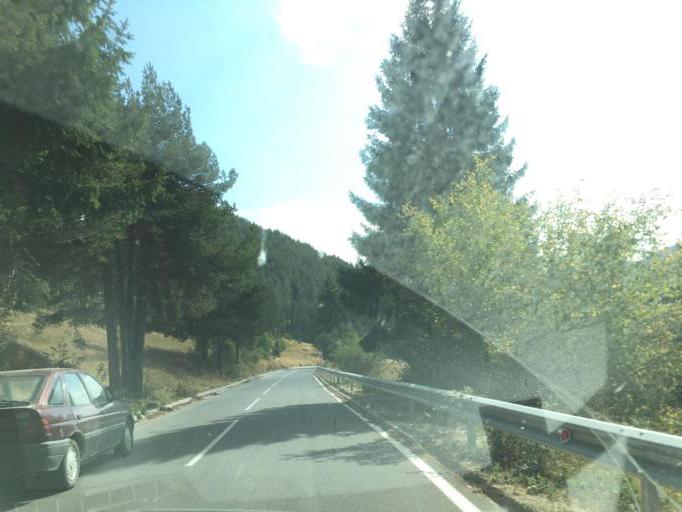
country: BG
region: Pazardzhik
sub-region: Obshtina Batak
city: Batak
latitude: 41.8910
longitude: 24.3294
